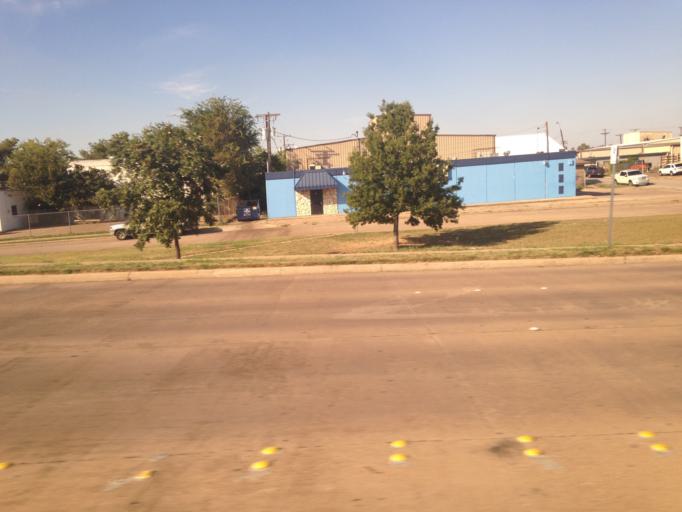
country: US
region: Texas
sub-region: Tarrant County
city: Fort Worth
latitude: 32.7060
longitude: -97.3274
